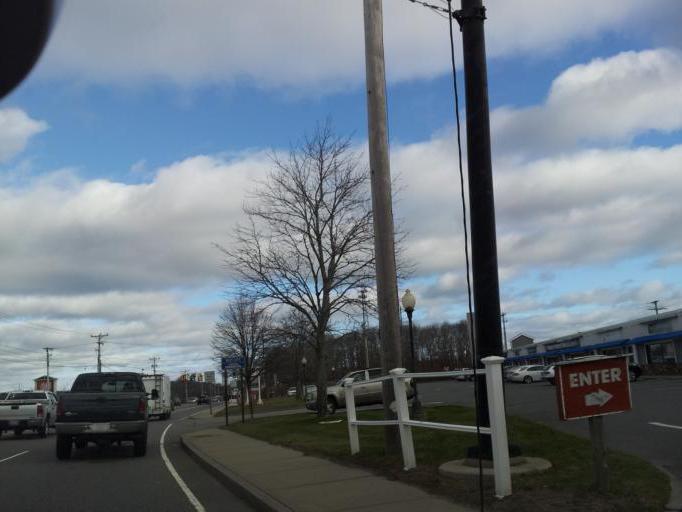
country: US
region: Massachusetts
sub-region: Plymouth County
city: Plymouth
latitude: 41.9315
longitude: -70.6585
